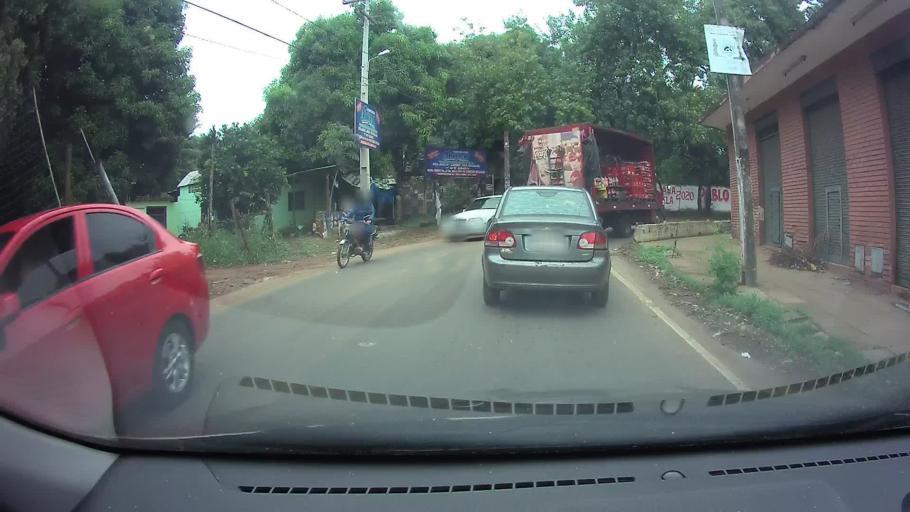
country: PY
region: Central
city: San Lorenzo
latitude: -25.3279
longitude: -57.5042
